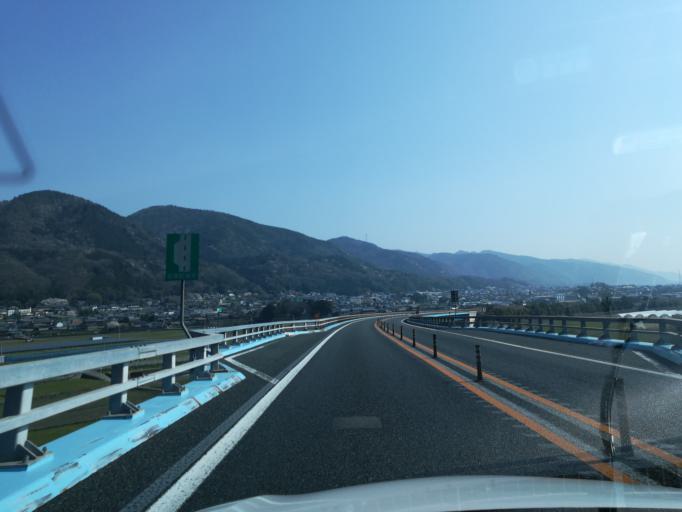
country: JP
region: Tokushima
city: Ikedacho
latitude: 34.0351
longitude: 133.8652
